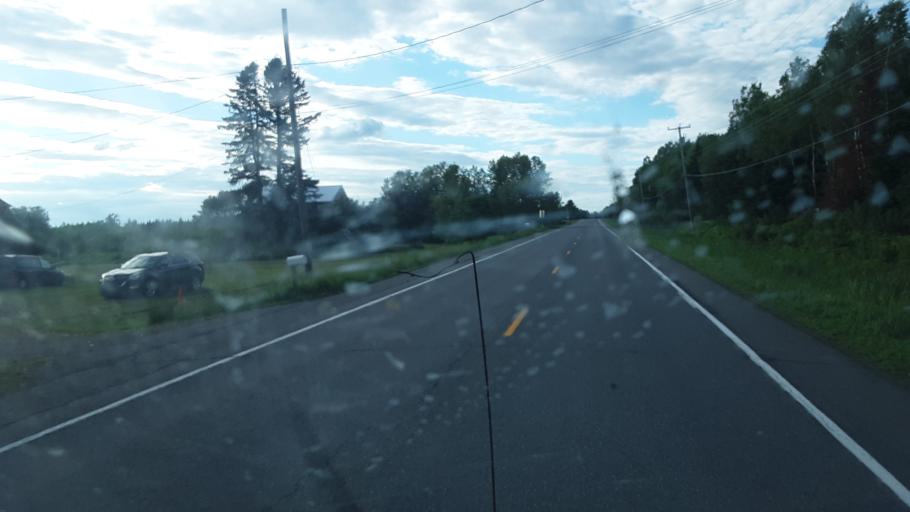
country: US
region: Maine
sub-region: Aroostook County
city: Presque Isle
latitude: 46.5651
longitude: -68.3772
